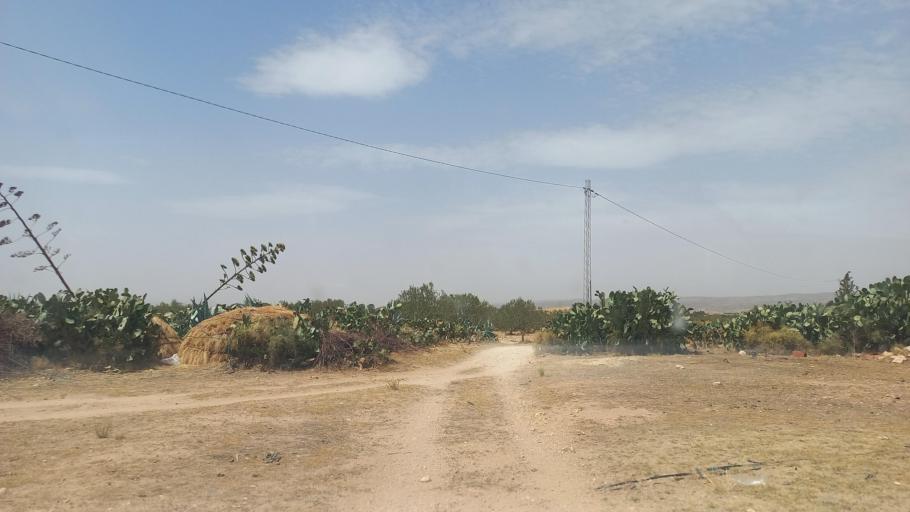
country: TN
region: Al Qasrayn
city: Kasserine
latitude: 35.2640
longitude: 8.9862
